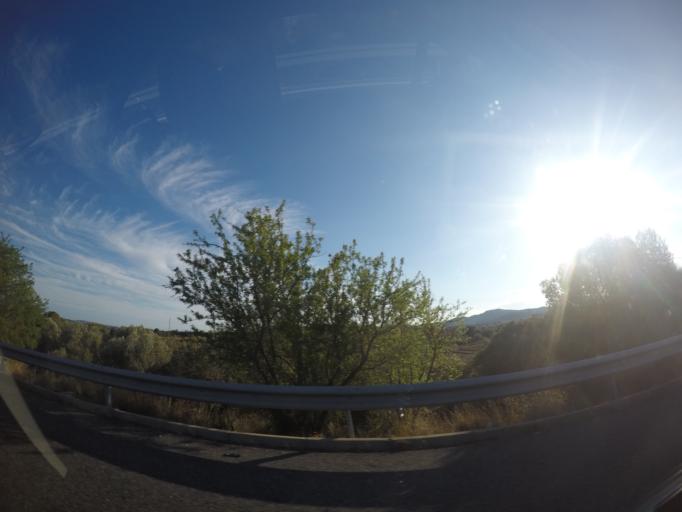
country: ES
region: Catalonia
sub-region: Provincia de Tarragona
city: Santa Oliva
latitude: 41.2731
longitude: 1.5244
